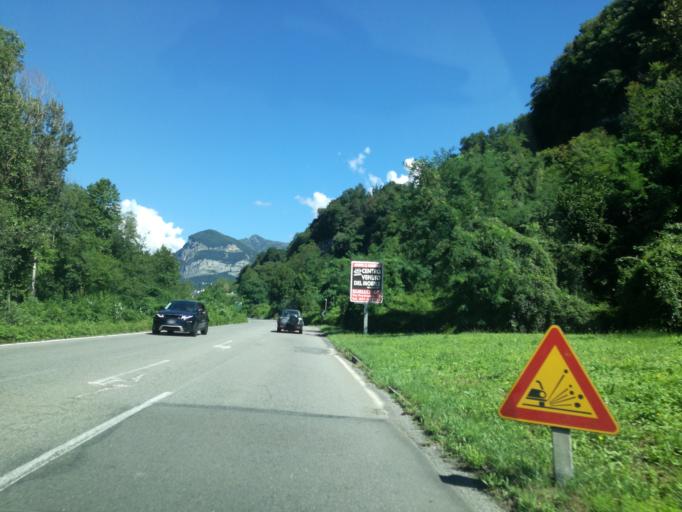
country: IT
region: Lombardy
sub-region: Provincia di Lecco
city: Monte Marenzo
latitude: 45.7735
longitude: 9.4435
